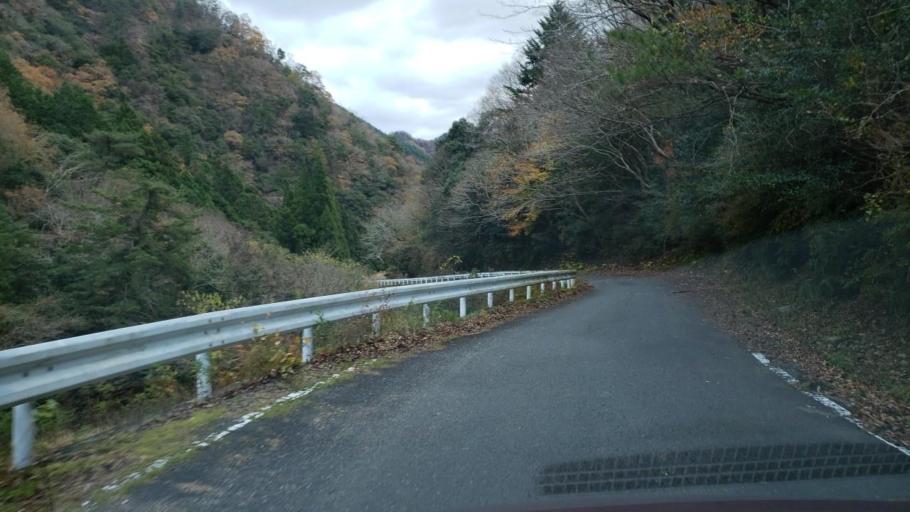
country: JP
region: Tokushima
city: Wakimachi
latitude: 34.1461
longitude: 134.2283
